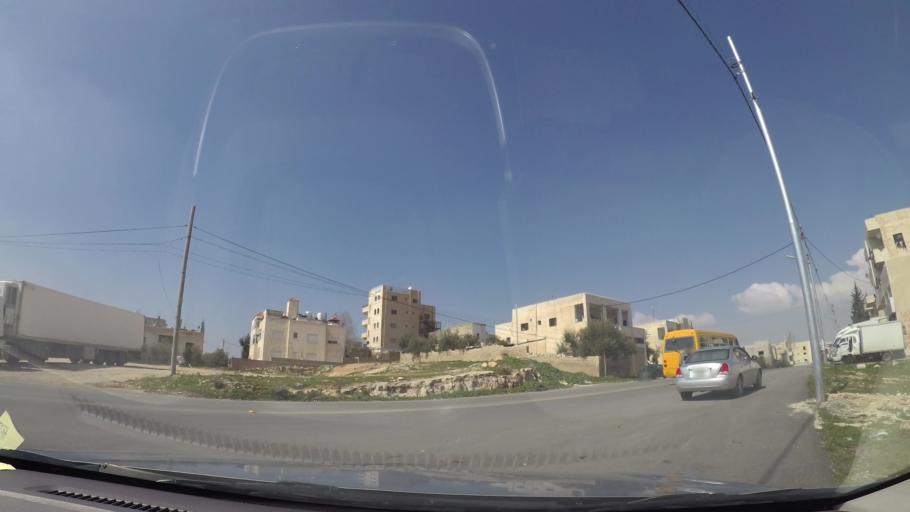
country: JO
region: Amman
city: Al Bunayyat ash Shamaliyah
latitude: 31.9004
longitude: 35.8998
